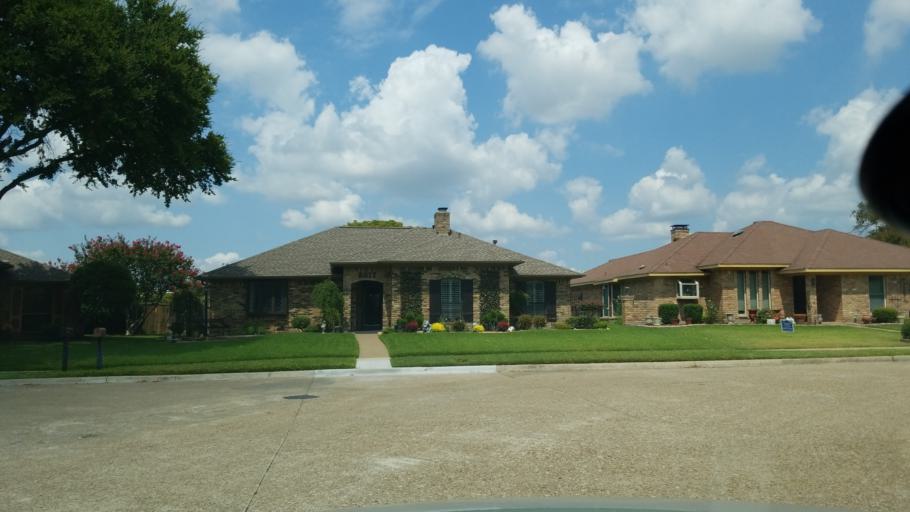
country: US
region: Texas
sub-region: Dallas County
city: Garland
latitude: 32.9291
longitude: -96.6584
